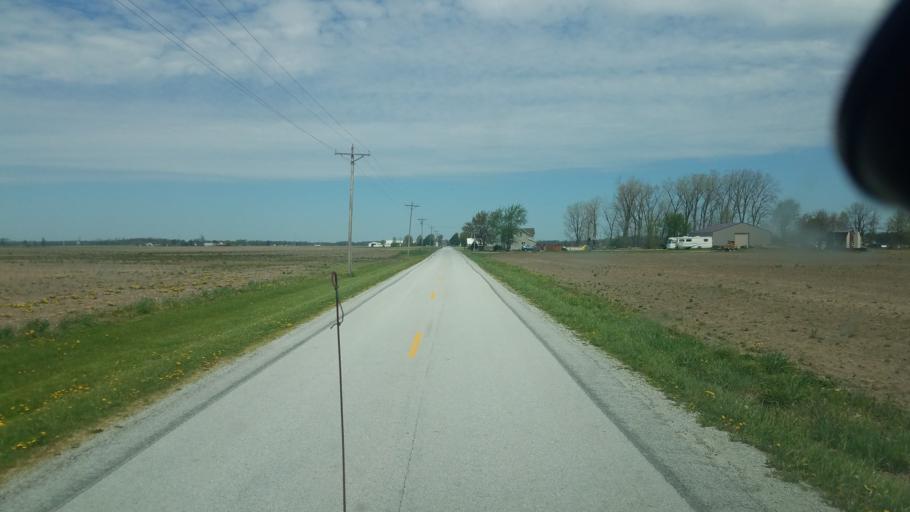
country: US
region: Ohio
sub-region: Hardin County
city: Kenton
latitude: 40.6550
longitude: -83.7256
